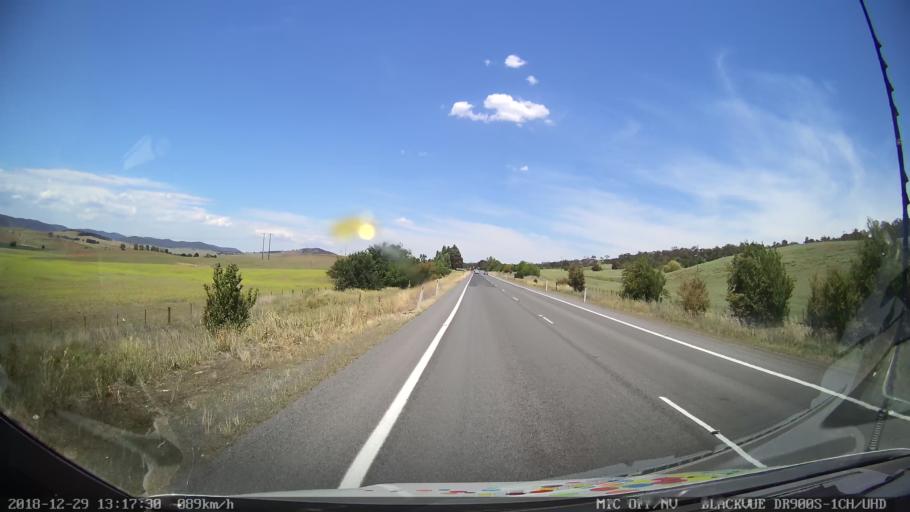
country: AU
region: Australian Capital Territory
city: Macarthur
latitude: -35.7384
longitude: 149.1607
